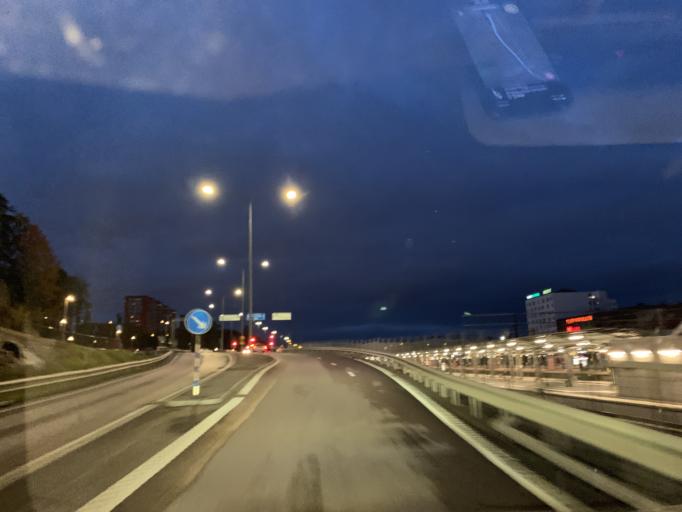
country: SE
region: Stockholm
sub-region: Huddinge Kommun
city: Huddinge
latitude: 59.2182
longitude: 17.9451
